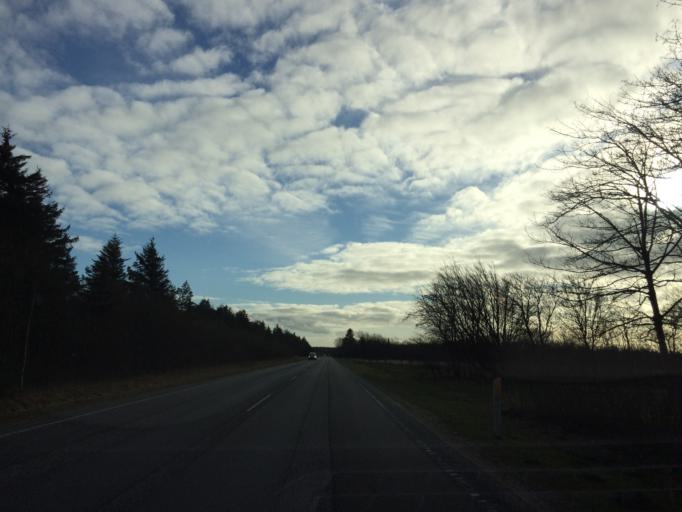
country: DK
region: Central Jutland
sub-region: Lemvig Kommune
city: Lemvig
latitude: 56.4887
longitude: 8.2994
